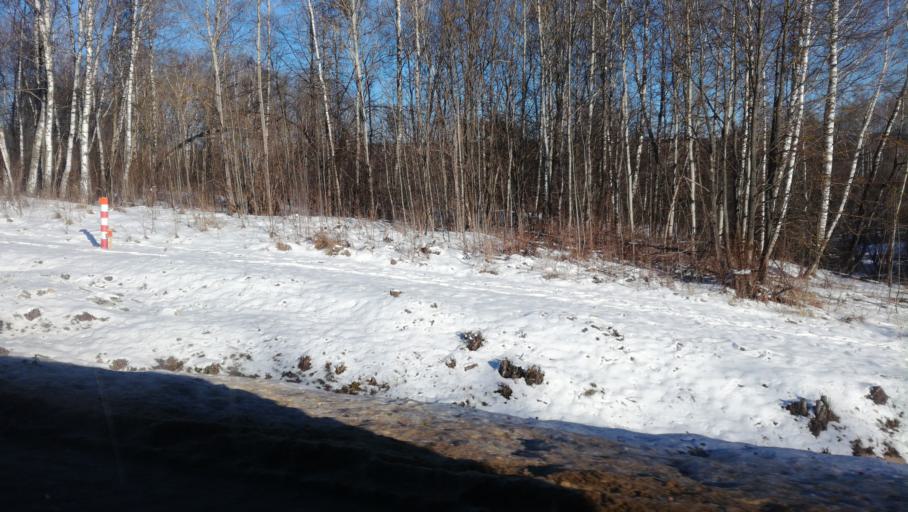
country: RU
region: Tula
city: Kosaya Gora
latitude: 54.1673
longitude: 37.4617
